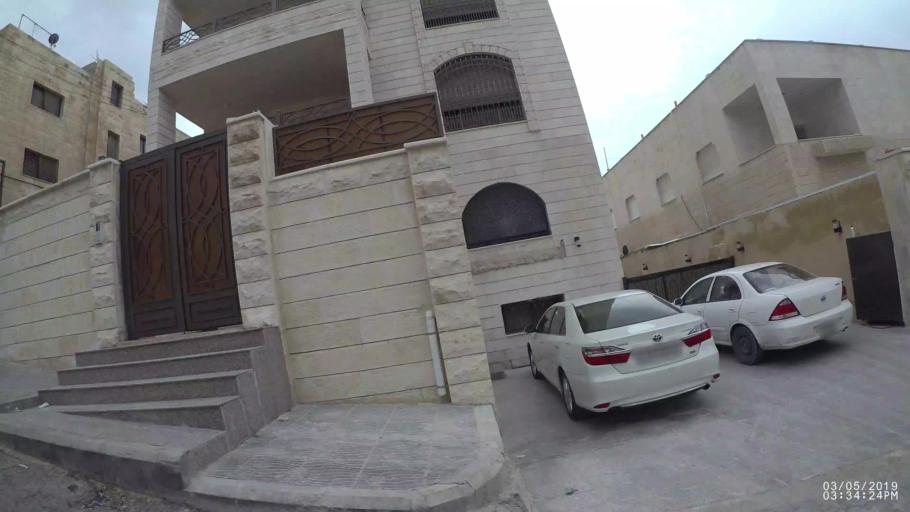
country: JO
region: Amman
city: Amman
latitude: 32.0057
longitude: 35.9467
